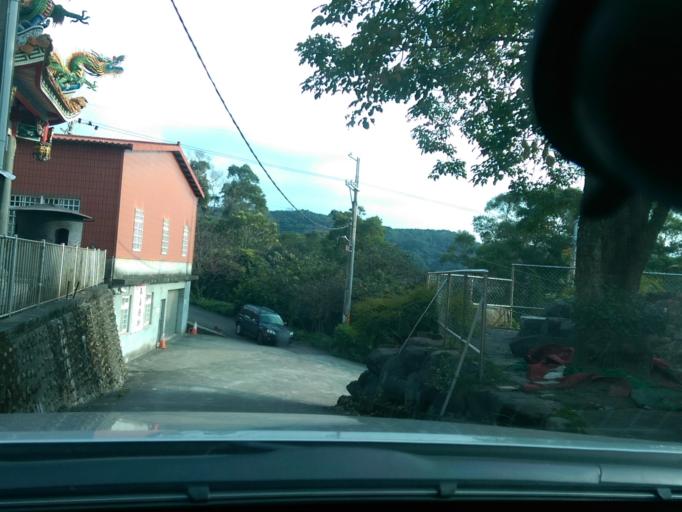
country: TW
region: Taiwan
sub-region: Taoyuan
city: Taoyuan
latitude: 25.0918
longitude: 121.3574
